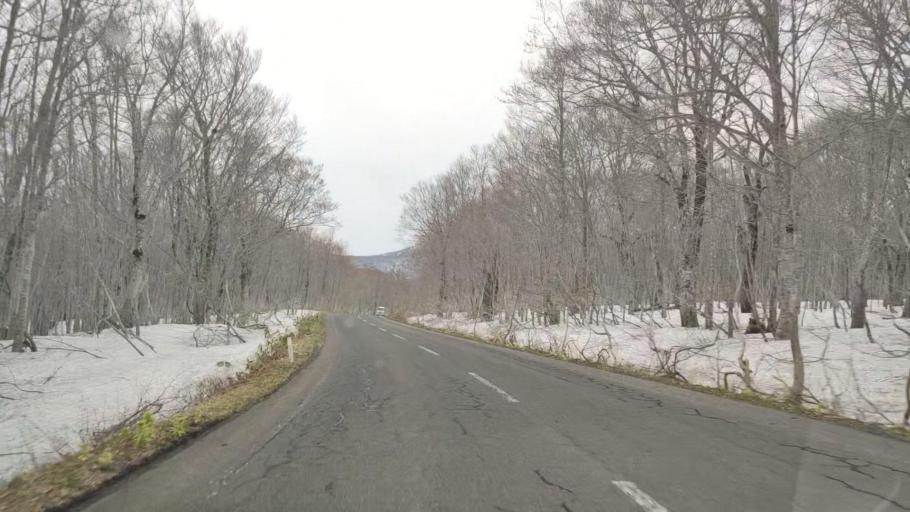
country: JP
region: Aomori
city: Aomori Shi
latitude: 40.6381
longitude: 140.9312
